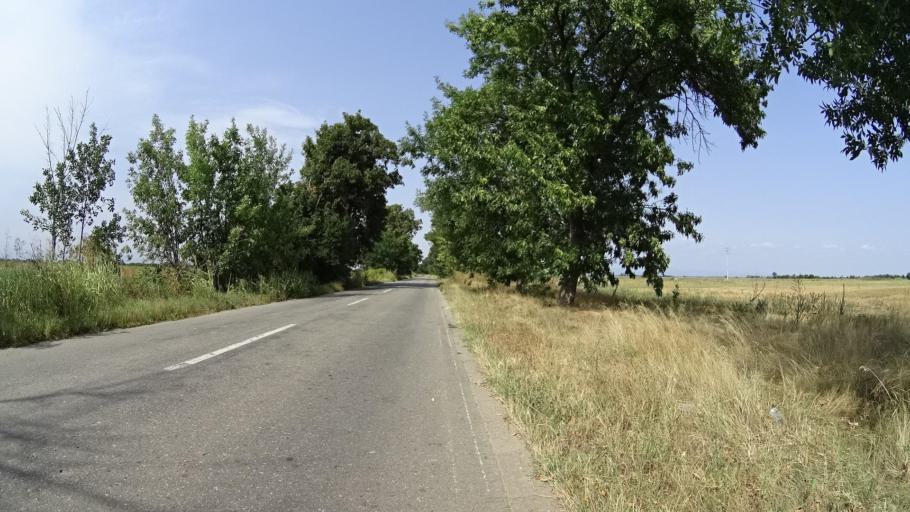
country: BG
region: Plovdiv
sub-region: Obshtina Plovdiv
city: Plovdiv
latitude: 42.2536
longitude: 24.7984
